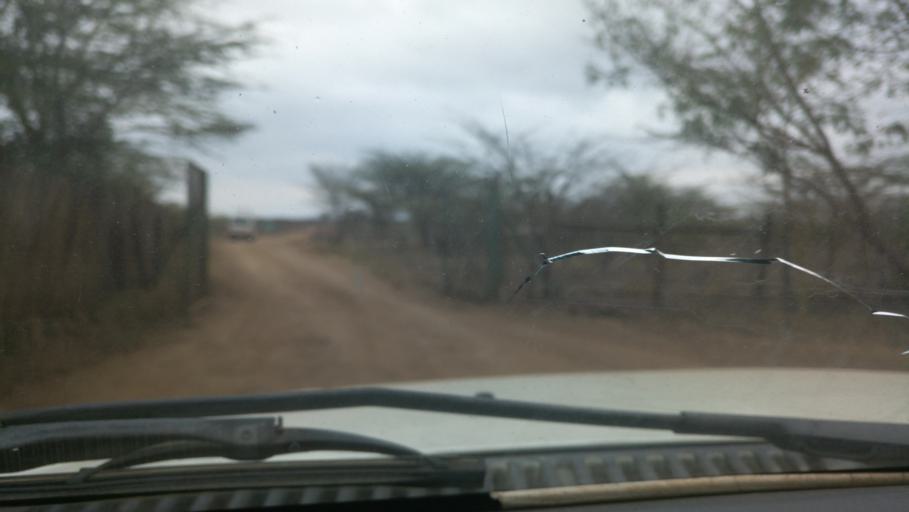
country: KE
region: Nairobi Area
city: Pumwani
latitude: -1.3386
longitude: 36.8653
